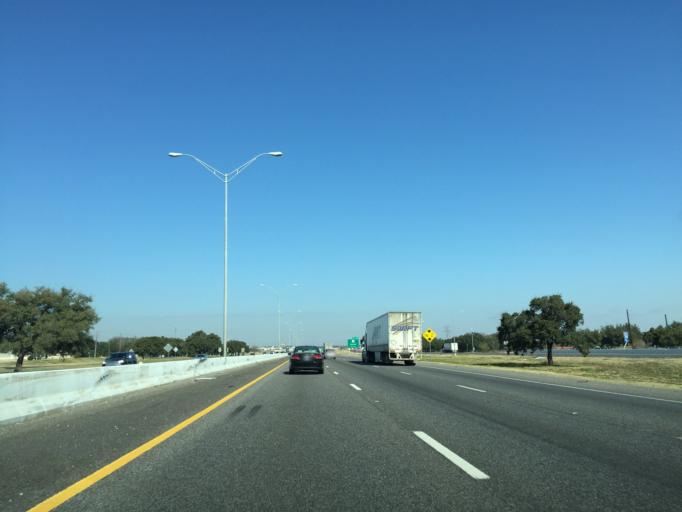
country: US
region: Texas
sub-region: Williamson County
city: Georgetown
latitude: 30.6133
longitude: -97.6874
